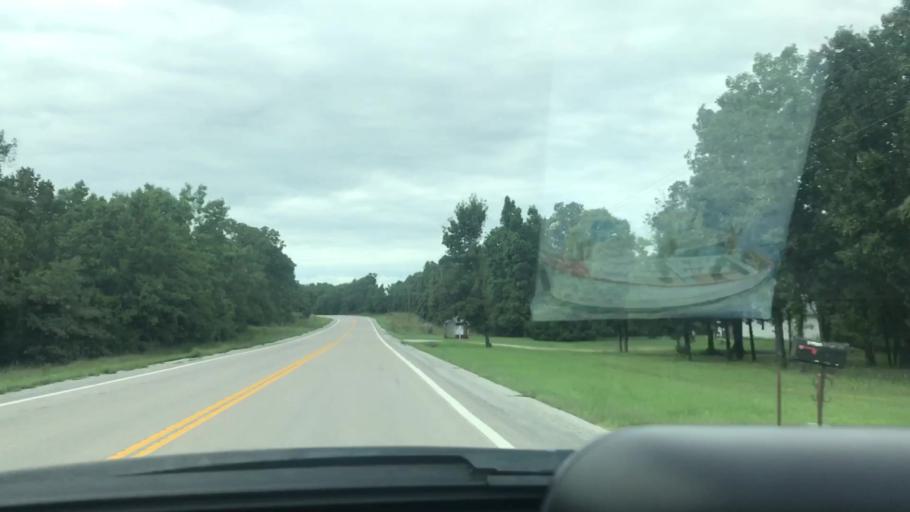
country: US
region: Missouri
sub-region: Benton County
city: Warsaw
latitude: 38.1566
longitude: -93.2969
